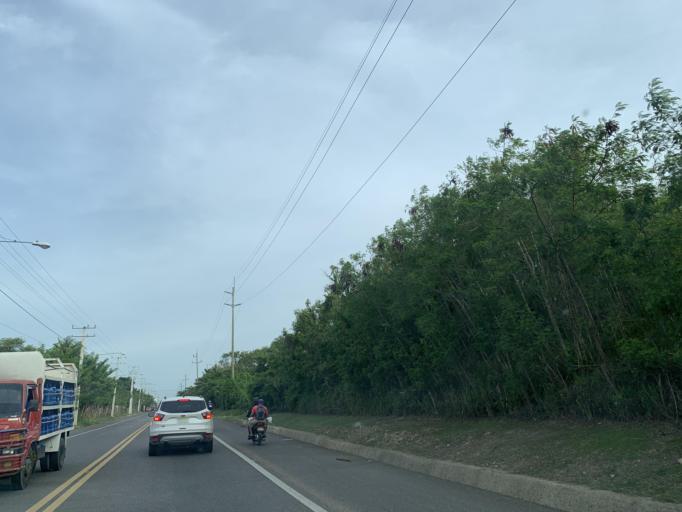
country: DO
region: Puerto Plata
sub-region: Puerto Plata
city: Puerto Plata
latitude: 19.7321
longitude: -70.6275
